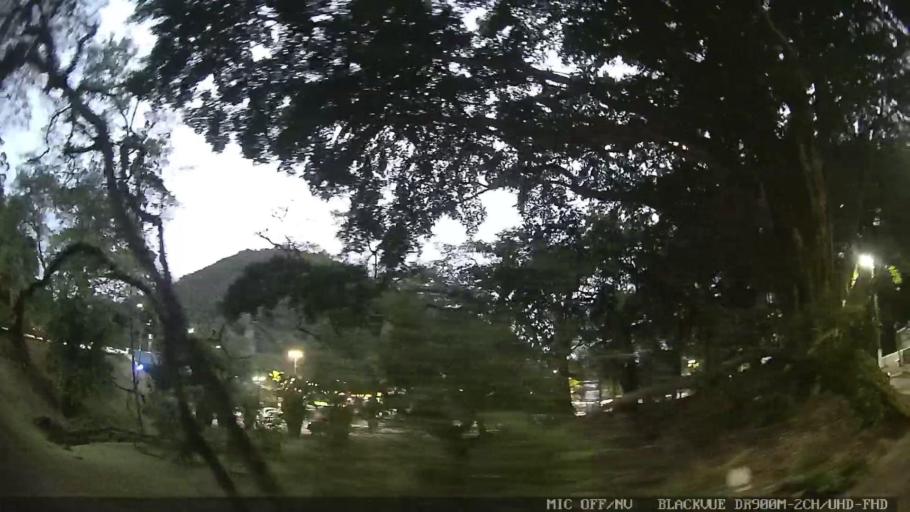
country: BR
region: Sao Paulo
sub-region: Guaruja
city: Guaruja
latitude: -23.9885
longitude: -46.2604
